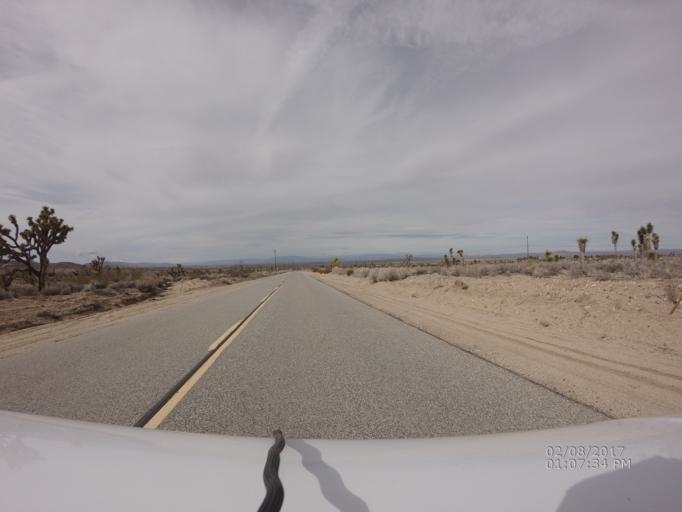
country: US
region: California
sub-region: Los Angeles County
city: Lake Los Angeles
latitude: 34.4749
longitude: -117.8331
